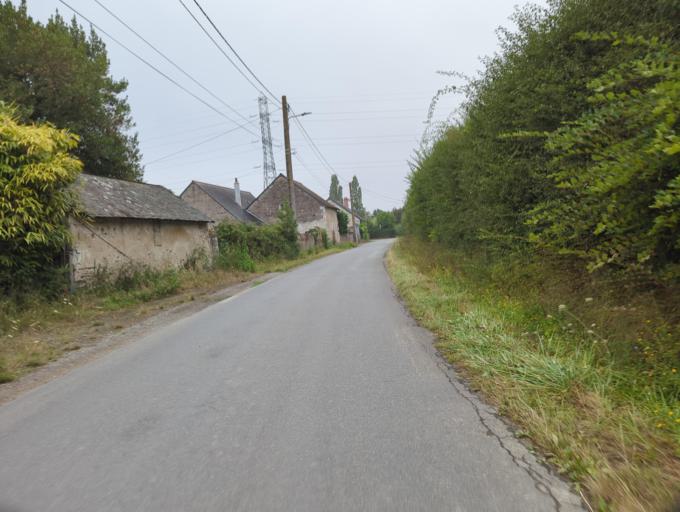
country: FR
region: Pays de la Loire
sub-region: Departement de Maine-et-Loire
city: Trelaze
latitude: 47.4809
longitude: -0.4787
